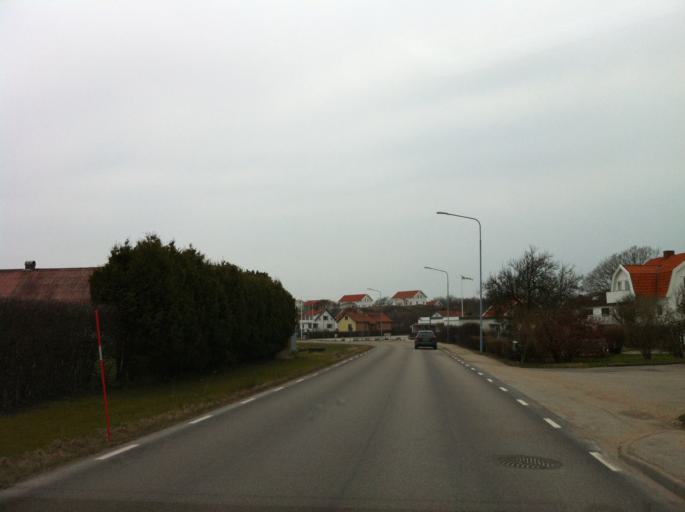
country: SE
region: Vaestra Goetaland
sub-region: Orust
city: Henan
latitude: 58.1755
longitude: 11.6976
